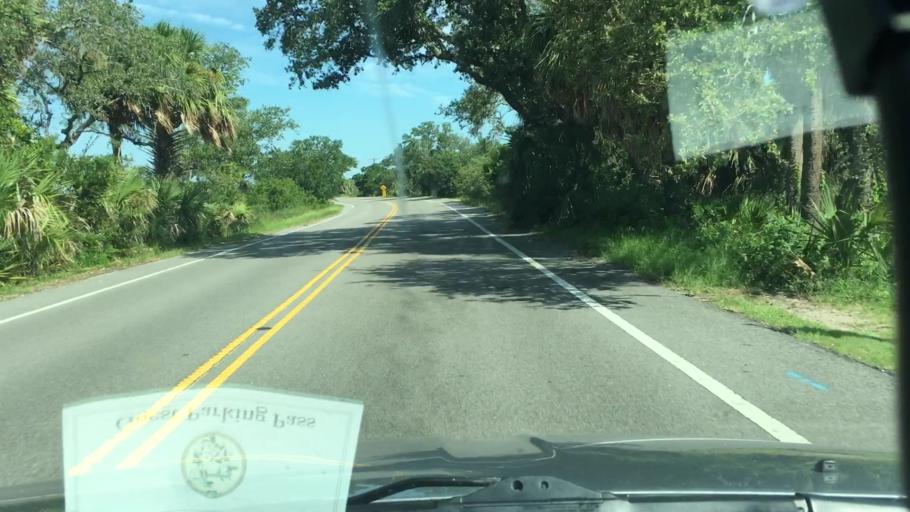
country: US
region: South Carolina
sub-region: Beaufort County
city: Beaufort
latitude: 32.3996
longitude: -80.4439
